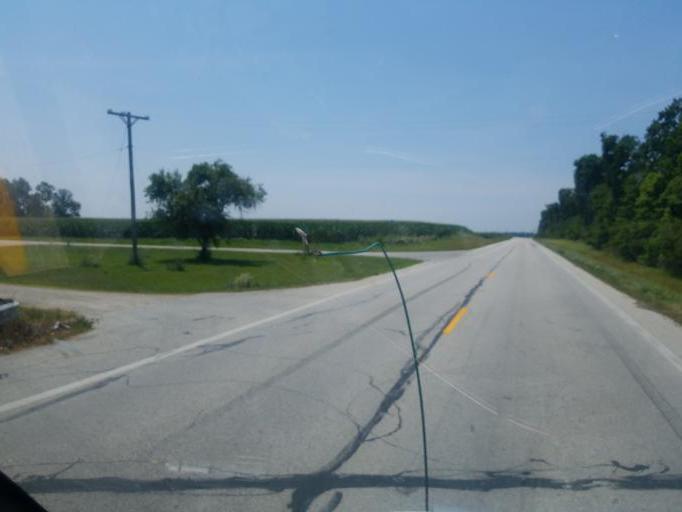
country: US
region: Ohio
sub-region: Shelby County
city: Fort Loramie
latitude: 40.3490
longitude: -84.3872
